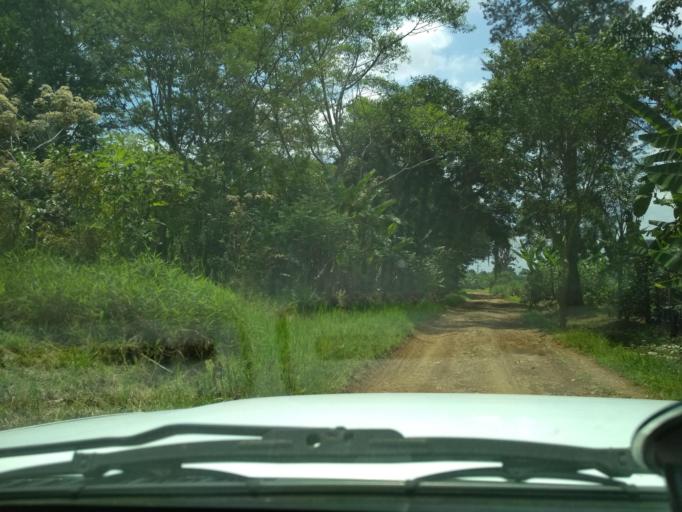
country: MX
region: Veracruz
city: Monte Blanco
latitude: 18.9585
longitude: -97.0175
